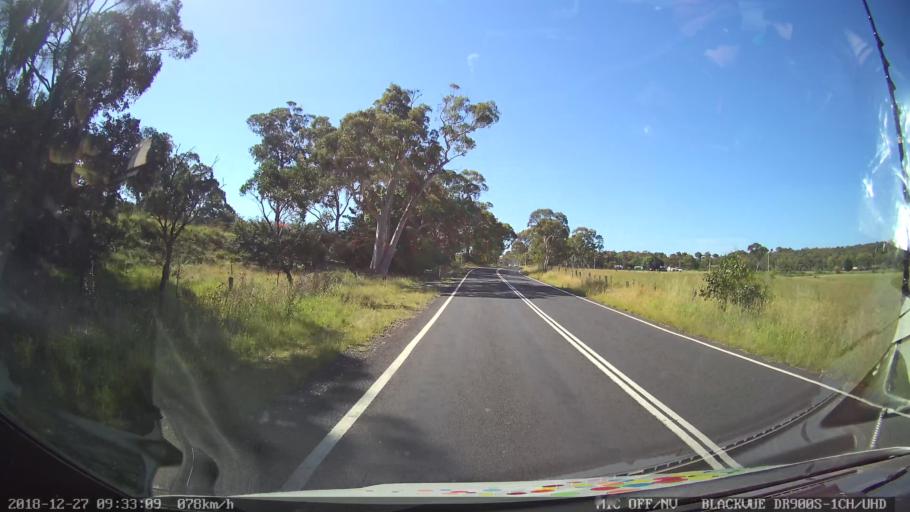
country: AU
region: New South Wales
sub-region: Lithgow
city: Portland
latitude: -33.2158
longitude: 150.0202
